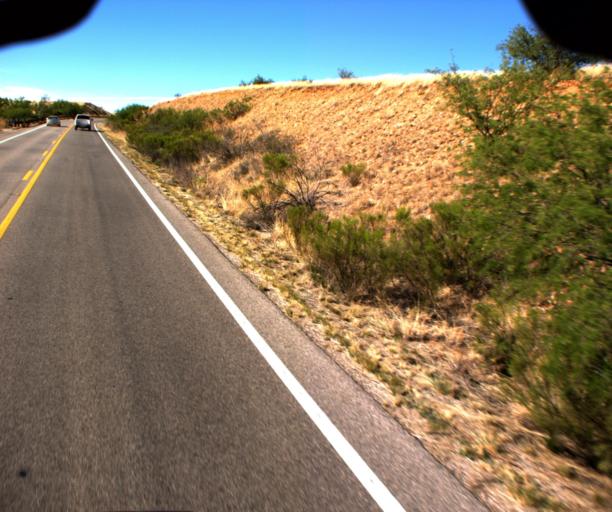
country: US
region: Arizona
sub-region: Pima County
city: Corona de Tucson
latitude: 31.7942
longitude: -110.7010
